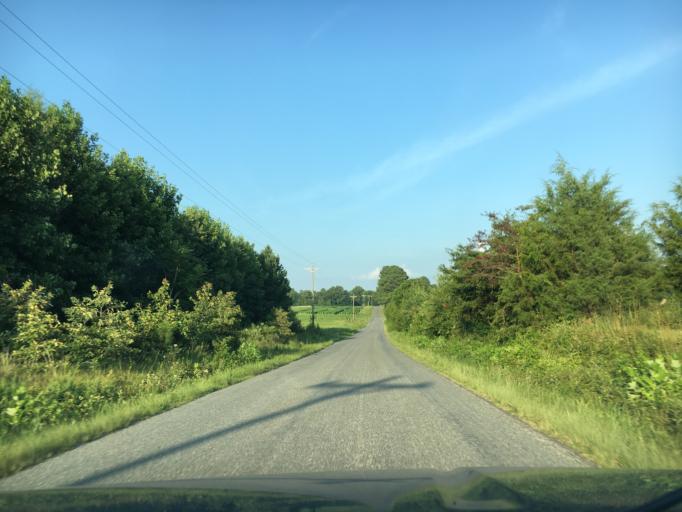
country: US
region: Virginia
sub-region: Pittsylvania County
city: Gretna
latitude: 36.8418
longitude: -79.1971
